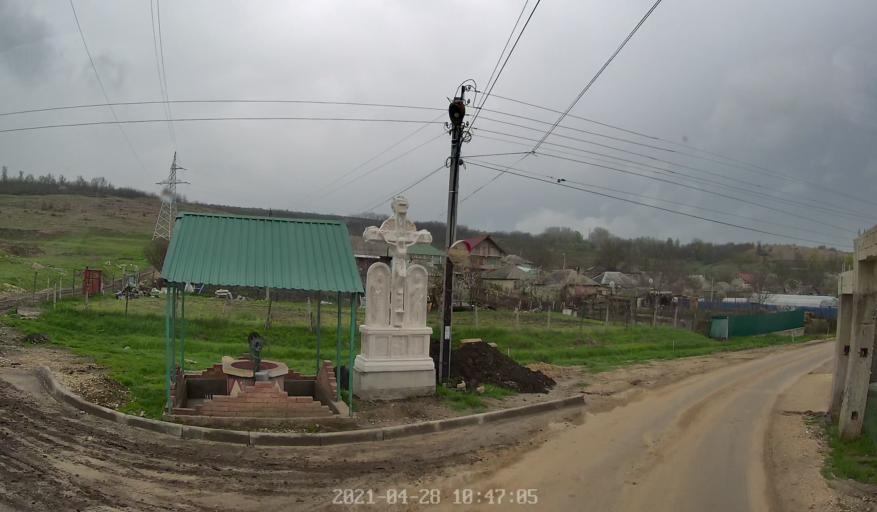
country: MD
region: Chisinau
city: Singera
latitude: 46.9908
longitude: 28.9479
